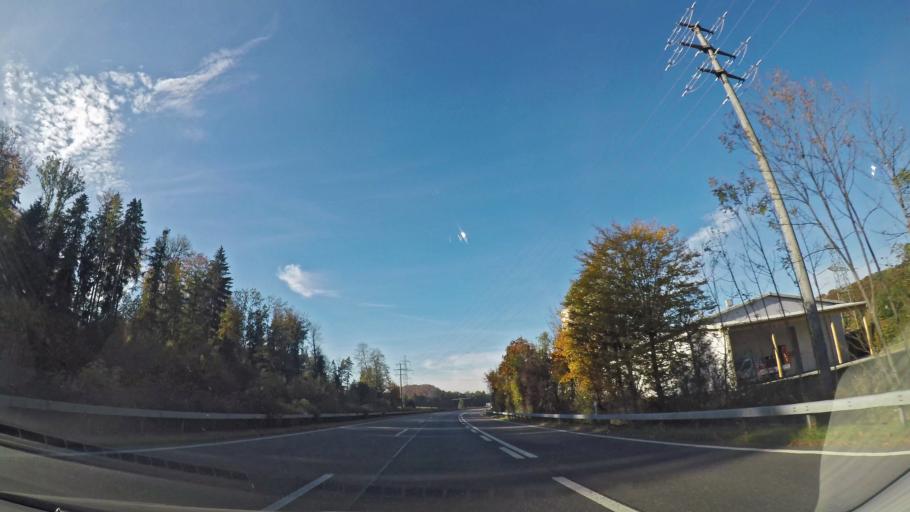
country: CH
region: Bern
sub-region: Frutigen-Niedersimmental District
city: Wimmis
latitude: 46.6974
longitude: 7.6402
